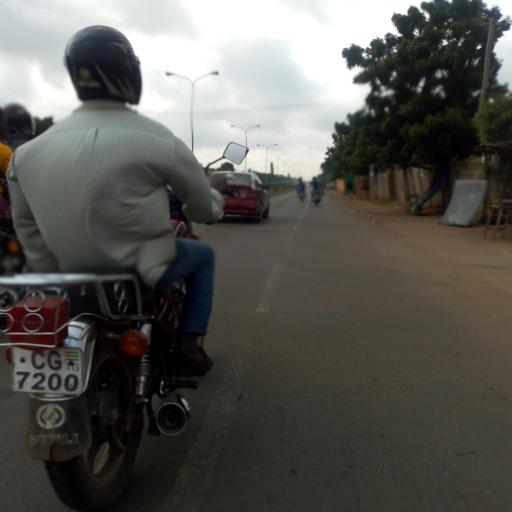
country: TG
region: Maritime
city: Lome
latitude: 6.1918
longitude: 1.2462
